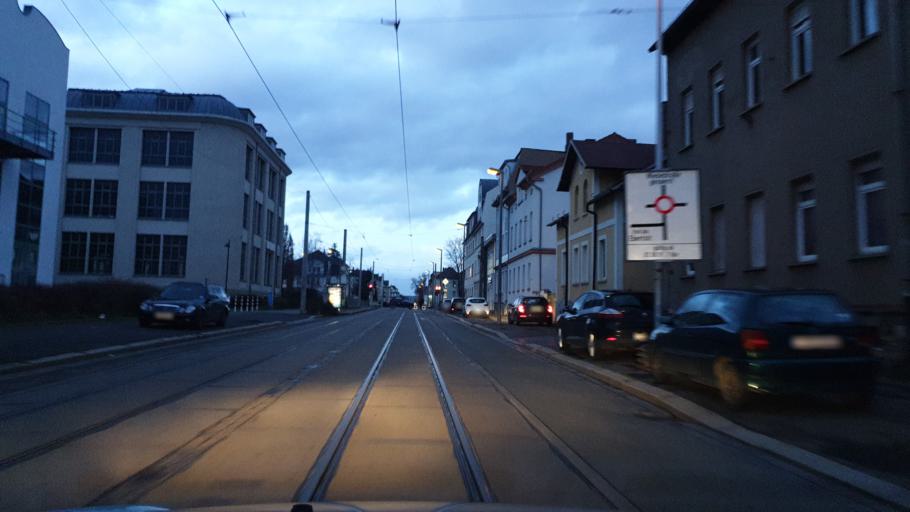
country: DE
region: Thuringia
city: Gera
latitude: 50.8539
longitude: 12.0728
